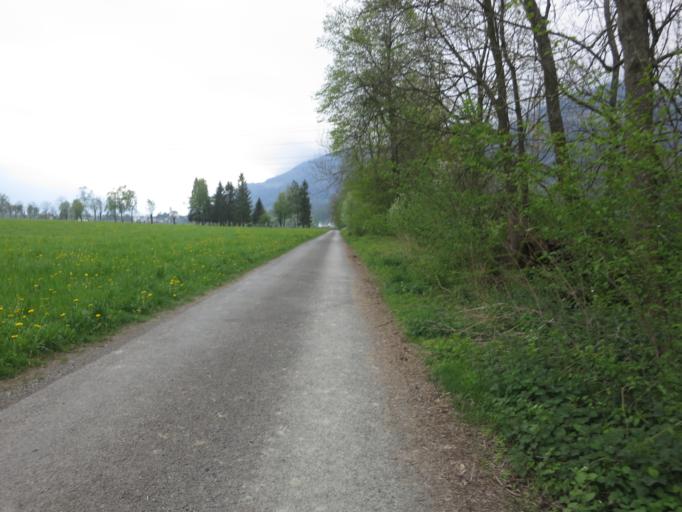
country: CH
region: Schwyz
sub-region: Bezirk March
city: Tuggen
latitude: 47.1808
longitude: 8.9515
